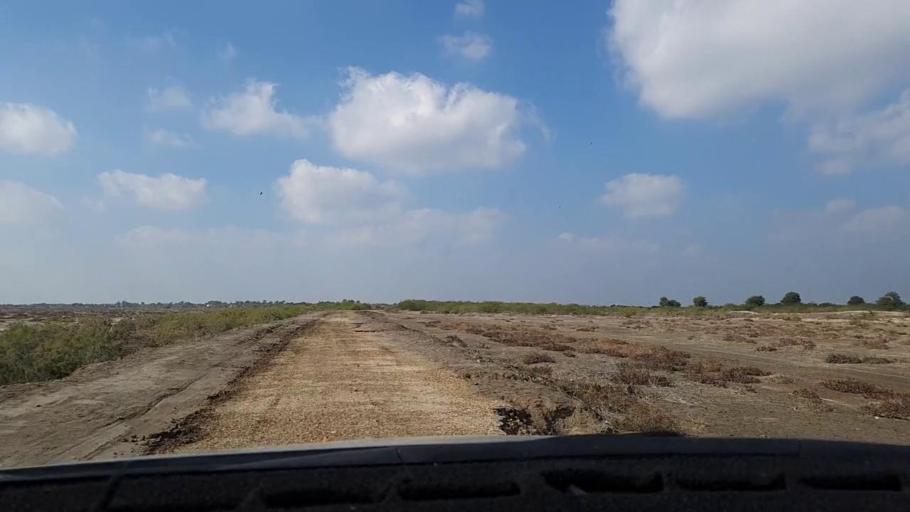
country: PK
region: Sindh
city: Tando Mittha Khan
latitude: 25.7688
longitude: 69.2649
